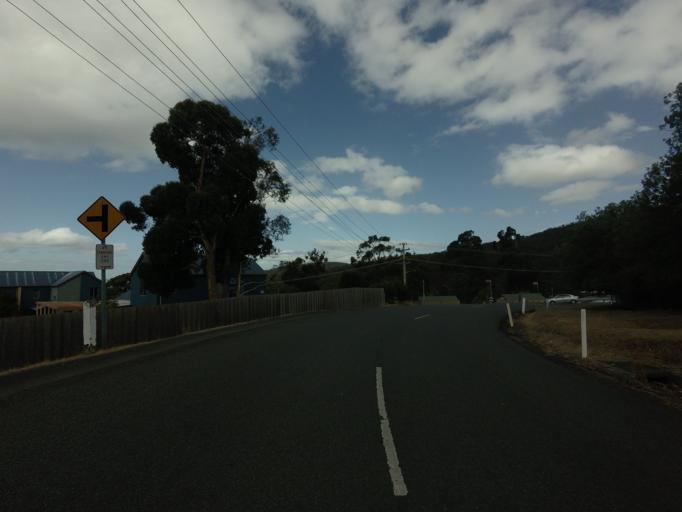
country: AU
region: Tasmania
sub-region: Hobart
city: Dynnyrne
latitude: -42.8995
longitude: 147.2754
